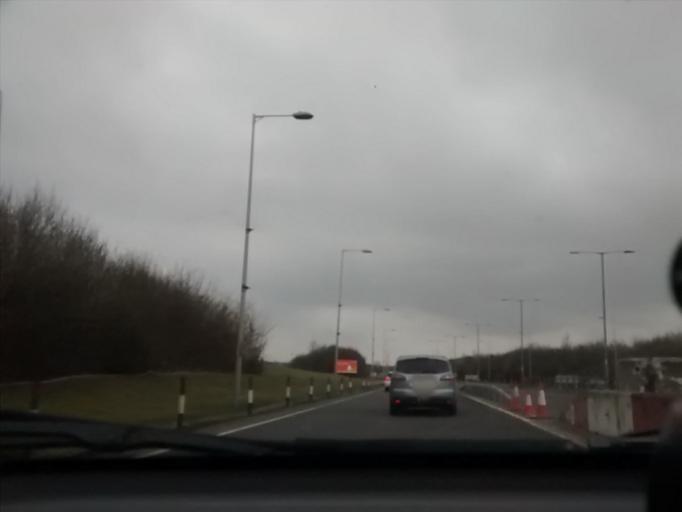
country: GB
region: England
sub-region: Essex
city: Takeley
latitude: 51.8799
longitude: 0.2505
